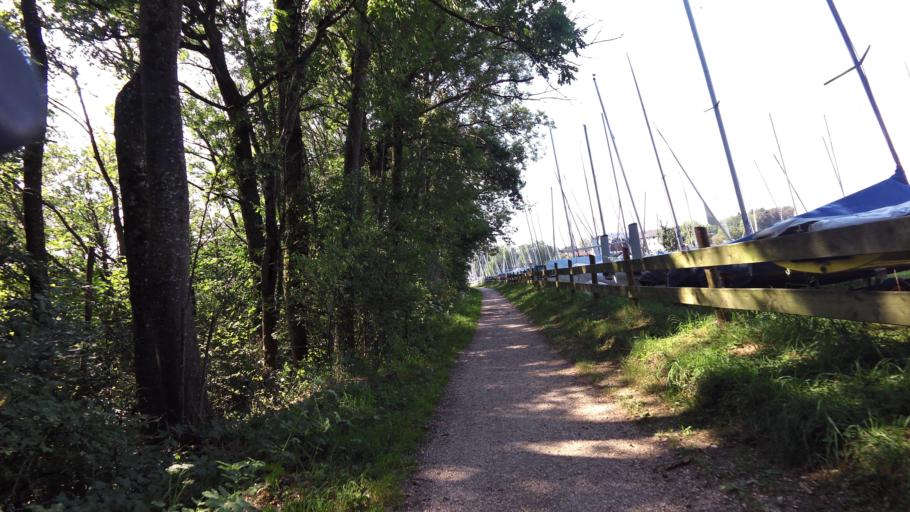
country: DE
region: Bavaria
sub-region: Upper Bavaria
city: Chieming
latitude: 47.9045
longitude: 12.5102
